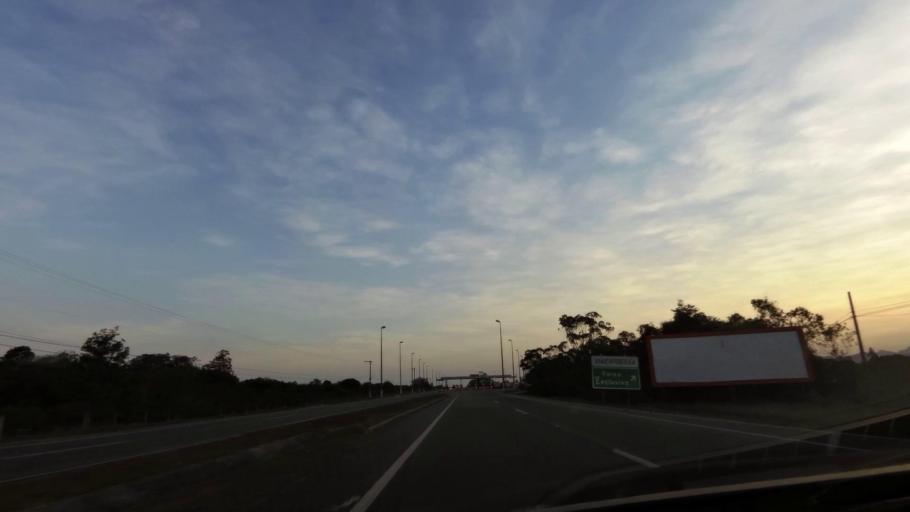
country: BR
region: Espirito Santo
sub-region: Guarapari
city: Guarapari
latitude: -20.5398
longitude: -40.3909
